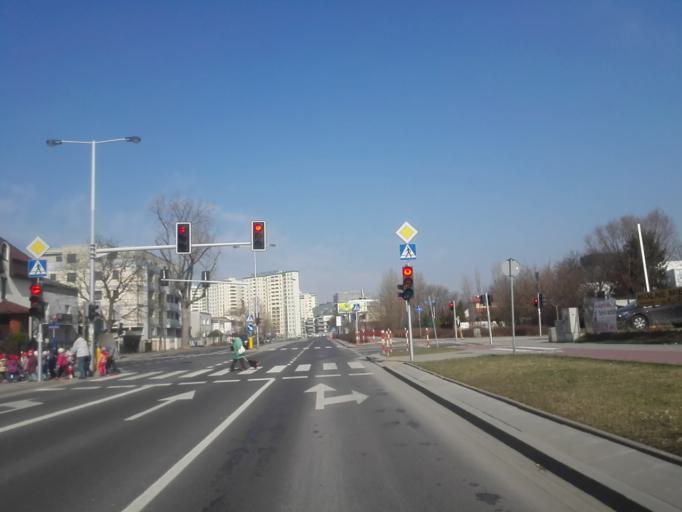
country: PL
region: Masovian Voivodeship
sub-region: Warszawa
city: Mokotow
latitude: 52.1758
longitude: 21.0268
